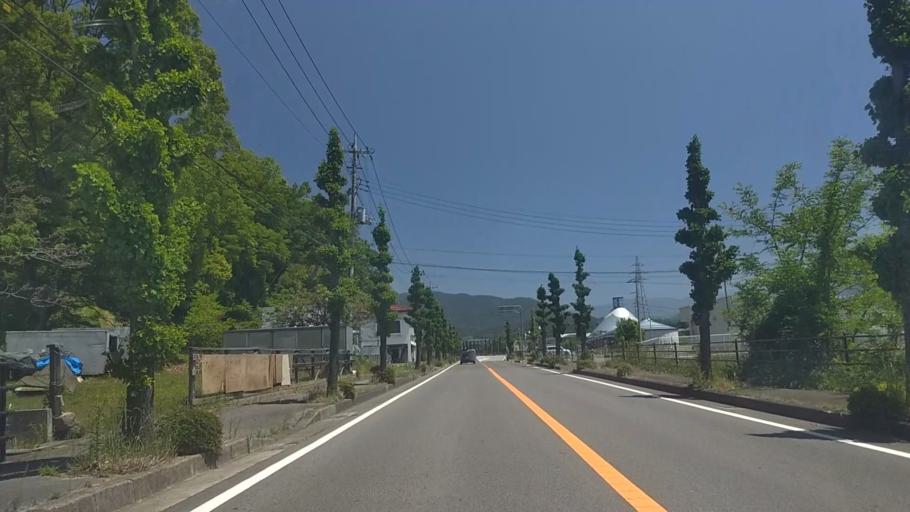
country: JP
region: Yamanashi
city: Nirasaki
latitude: 35.7950
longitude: 138.4220
